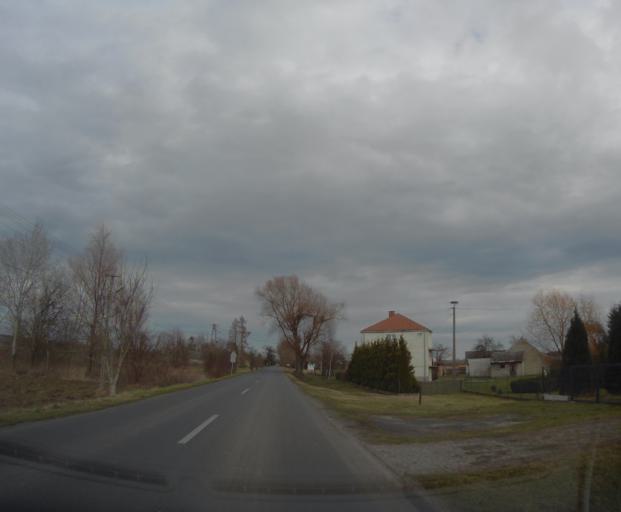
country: PL
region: Subcarpathian Voivodeship
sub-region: Powiat nizanski
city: Ulanow
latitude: 50.4759
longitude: 22.2515
